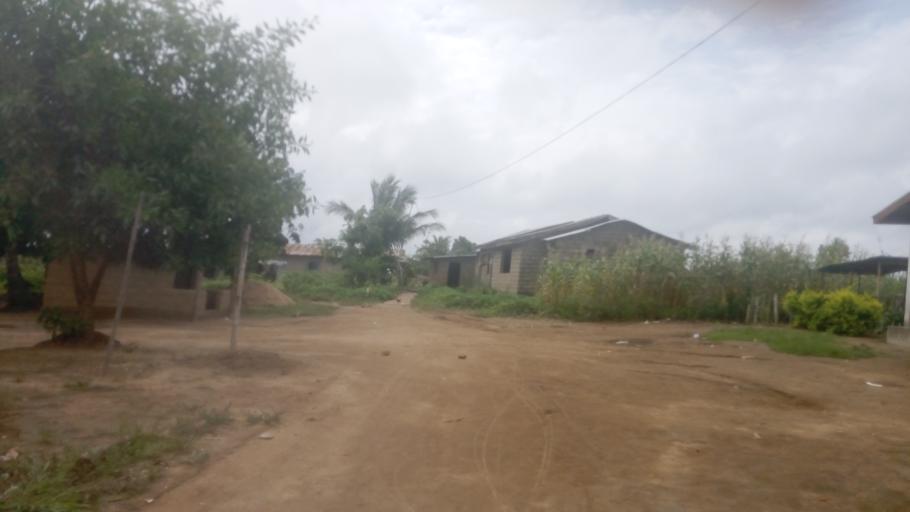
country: SL
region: Northern Province
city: Lunsar
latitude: 8.6939
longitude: -12.5403
